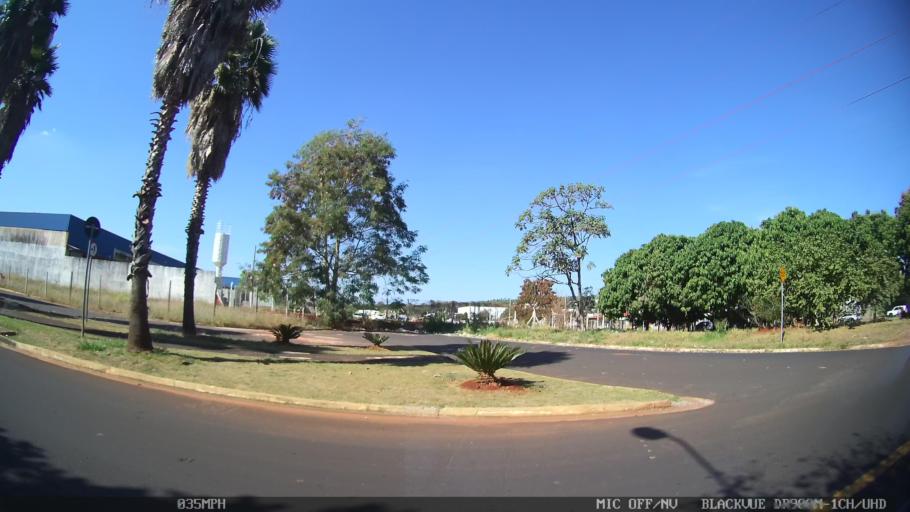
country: BR
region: Sao Paulo
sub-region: Ribeirao Preto
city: Ribeirao Preto
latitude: -21.2227
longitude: -47.7627
